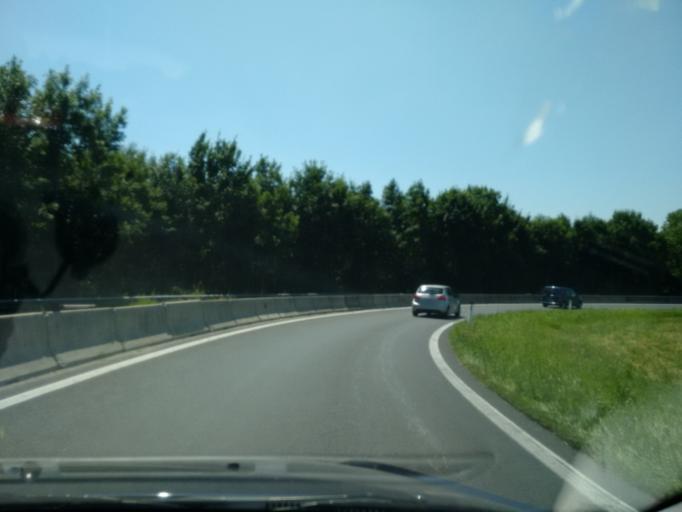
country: AT
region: Upper Austria
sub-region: Politischer Bezirk Vocklabruck
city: Attnang-Puchheim
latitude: 47.9550
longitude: 13.7326
